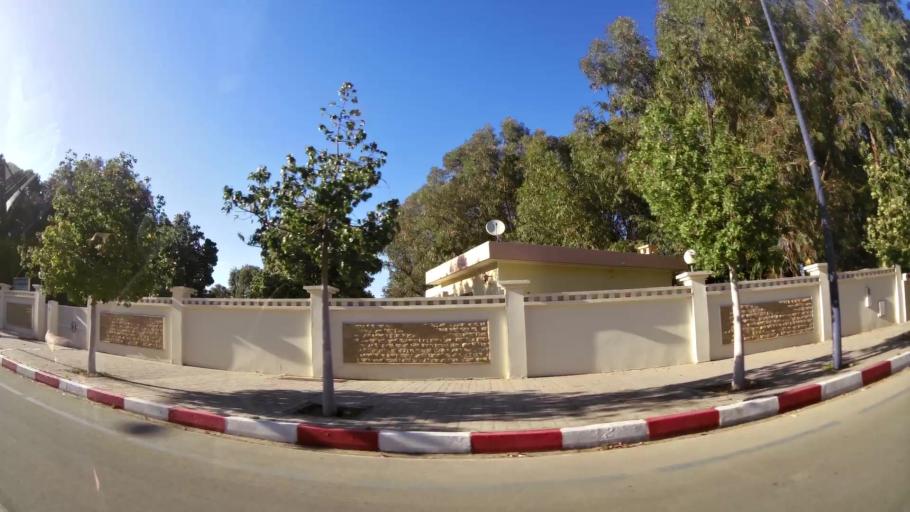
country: MA
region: Oriental
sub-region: Berkane-Taourirt
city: Madagh
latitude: 35.0874
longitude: -2.2355
